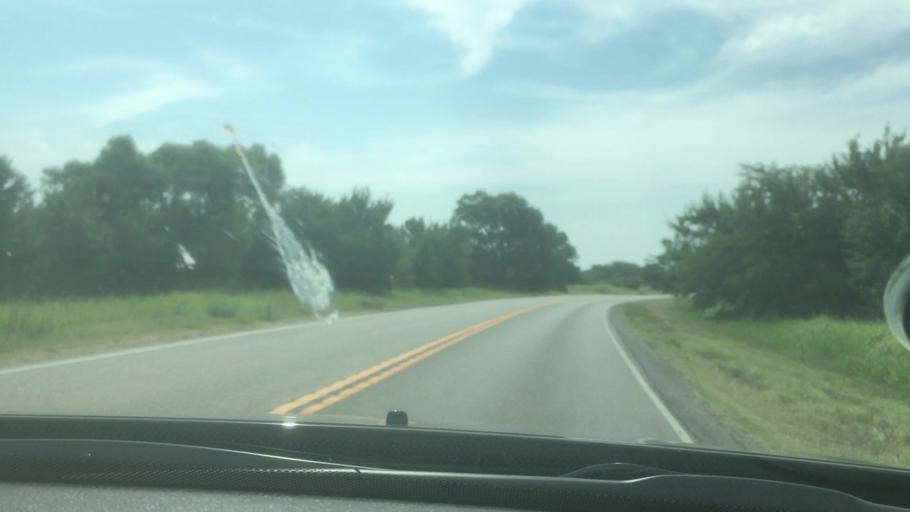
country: US
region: Oklahoma
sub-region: Garvin County
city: Maysville
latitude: 34.8118
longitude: -97.3798
